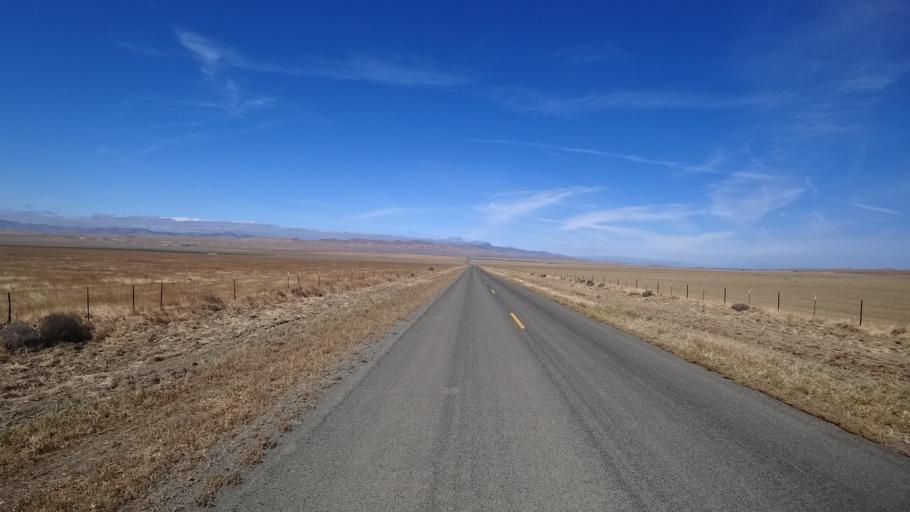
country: US
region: California
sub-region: Kings County
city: Kettleman City
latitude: 35.9353
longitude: -120.0228
